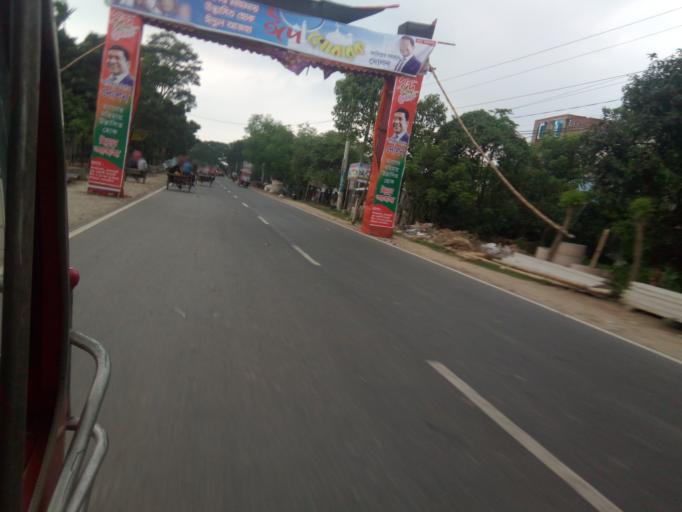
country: BD
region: Khulna
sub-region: Magura
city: Magura
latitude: 23.5427
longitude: 89.6251
